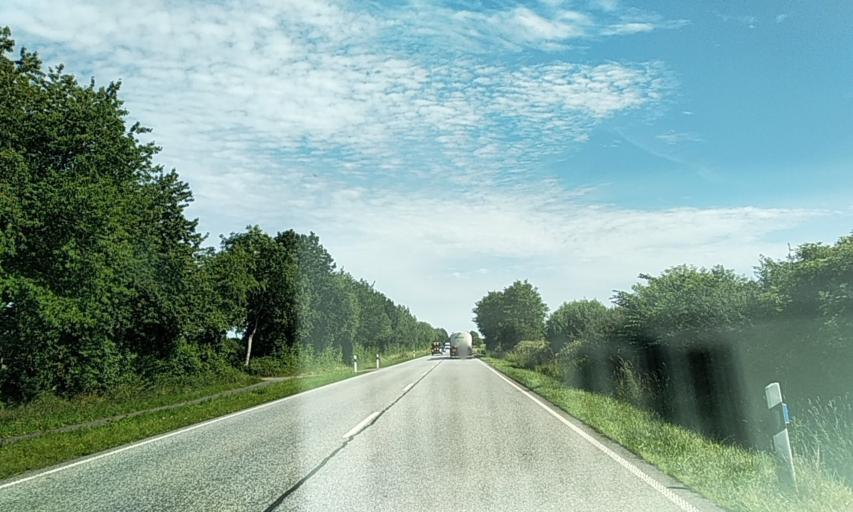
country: DE
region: Schleswig-Holstein
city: Kropp
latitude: 54.4223
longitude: 9.5306
